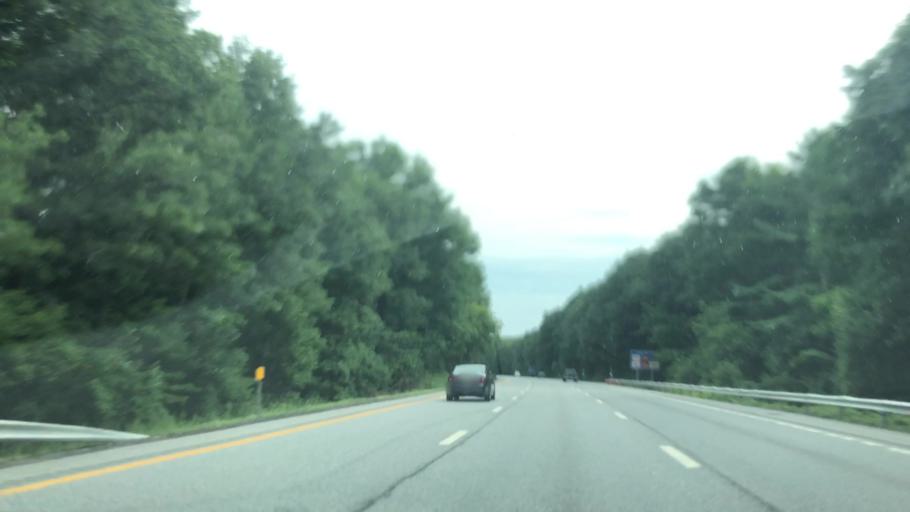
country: US
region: New York
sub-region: Saratoga County
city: Saratoga Springs
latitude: 43.1062
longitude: -73.7527
